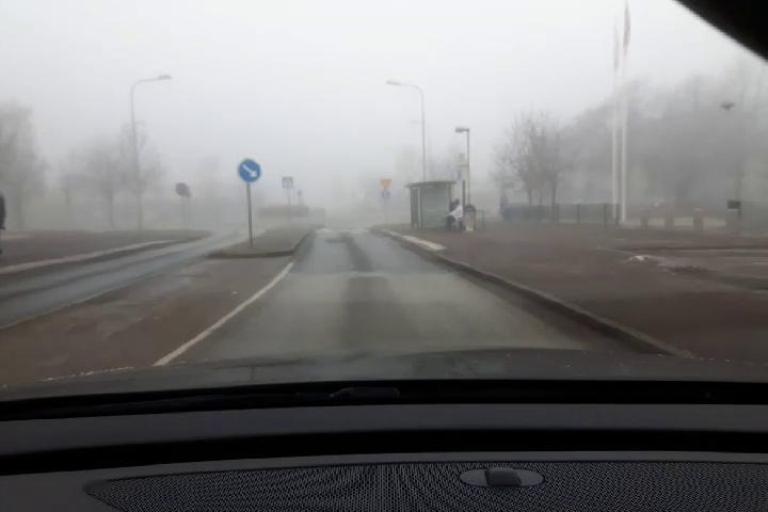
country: SE
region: Vaestra Goetaland
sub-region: Goteborg
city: Majorna
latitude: 57.6666
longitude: 11.8728
